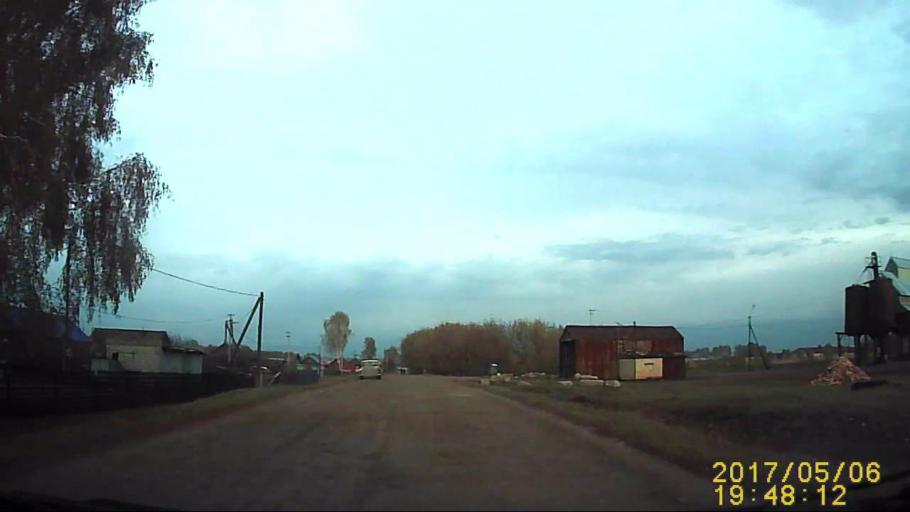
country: RU
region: Ulyanovsk
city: Staraya Mayna
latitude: 54.6018
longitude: 48.9212
